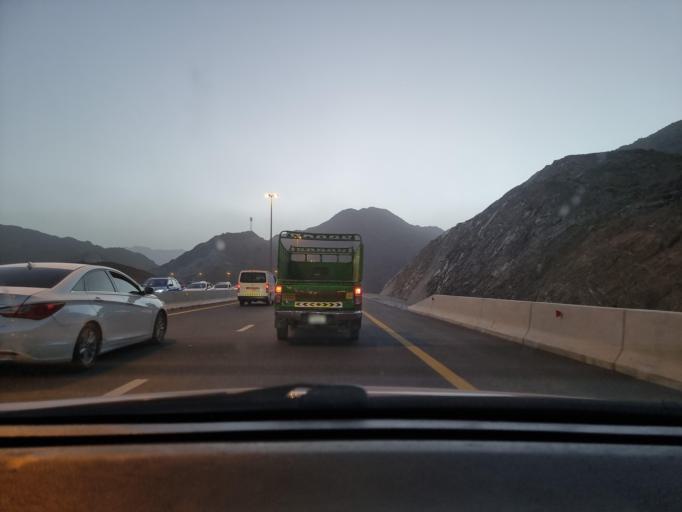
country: AE
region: Ash Shariqah
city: Khawr Fakkan
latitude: 25.3503
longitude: 56.3229
